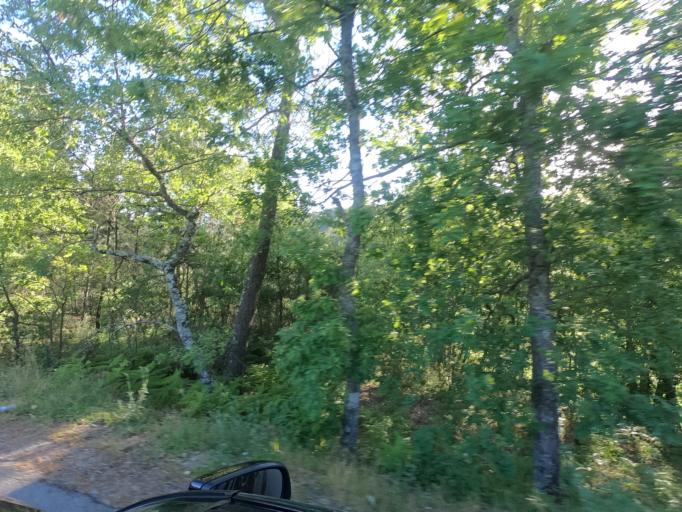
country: PT
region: Vila Real
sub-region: Vila Real
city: Vila Real
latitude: 41.3383
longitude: -7.7371
